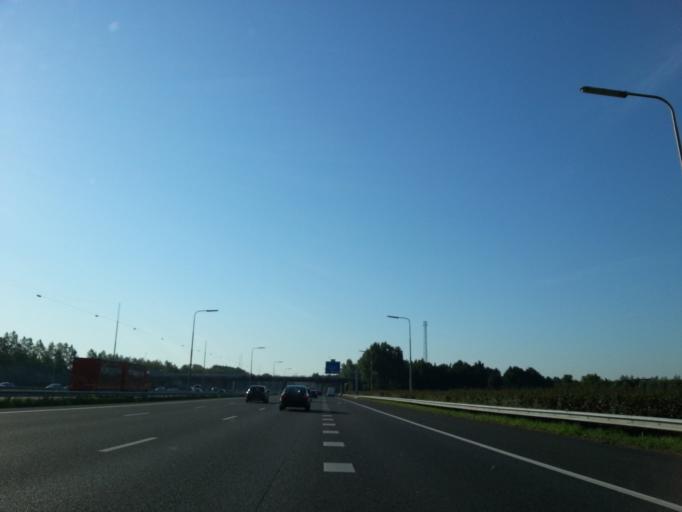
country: NL
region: South Holland
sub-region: Gemeente Ridderkerk
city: Ridderkerk
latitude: 51.8653
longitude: 4.5846
